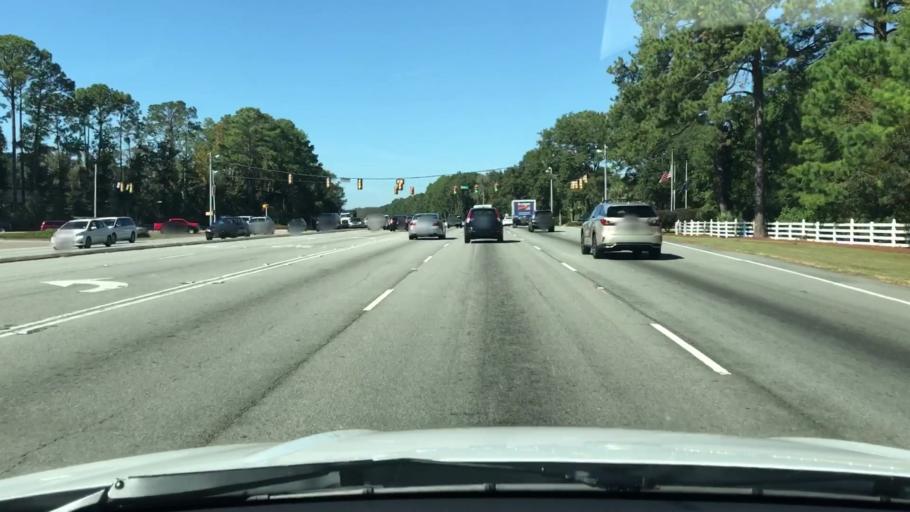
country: US
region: South Carolina
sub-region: Beaufort County
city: Bluffton
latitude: 32.2595
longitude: -80.8519
